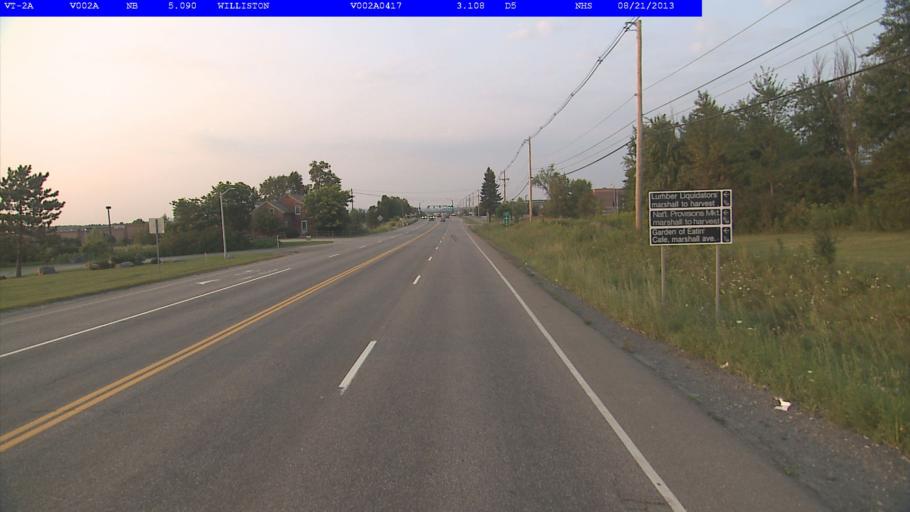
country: US
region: Vermont
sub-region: Chittenden County
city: Williston
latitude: 44.4410
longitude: -73.1140
